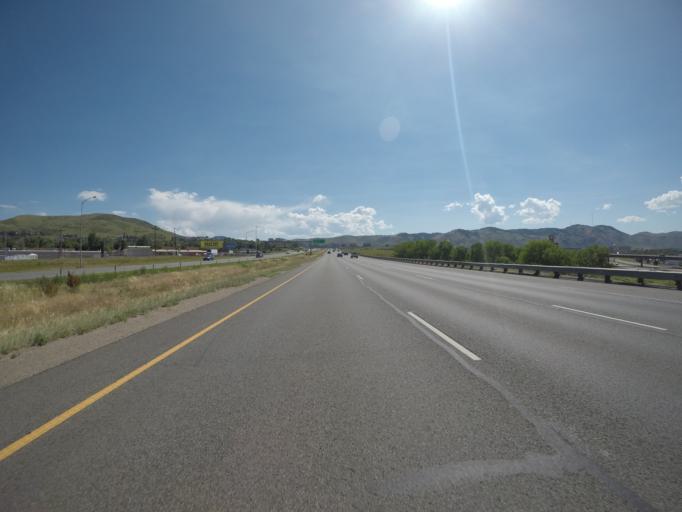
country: US
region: Colorado
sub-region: Jefferson County
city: West Pleasant View
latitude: 39.7247
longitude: -105.1805
